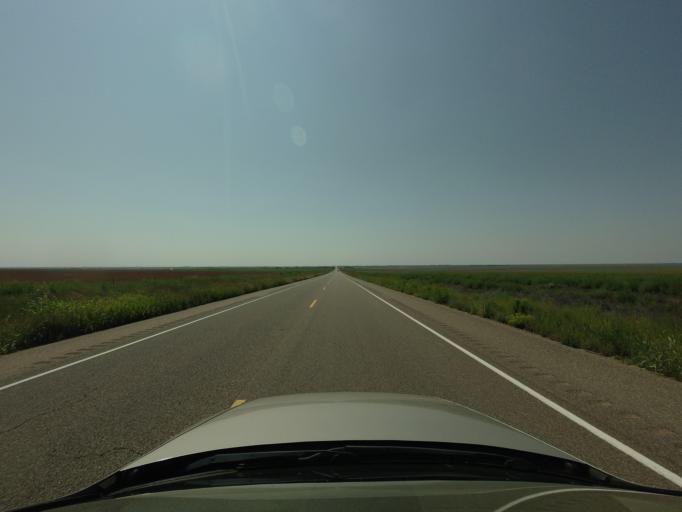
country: US
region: New Mexico
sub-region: Curry County
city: Clovis
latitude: 34.5478
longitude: -103.1965
